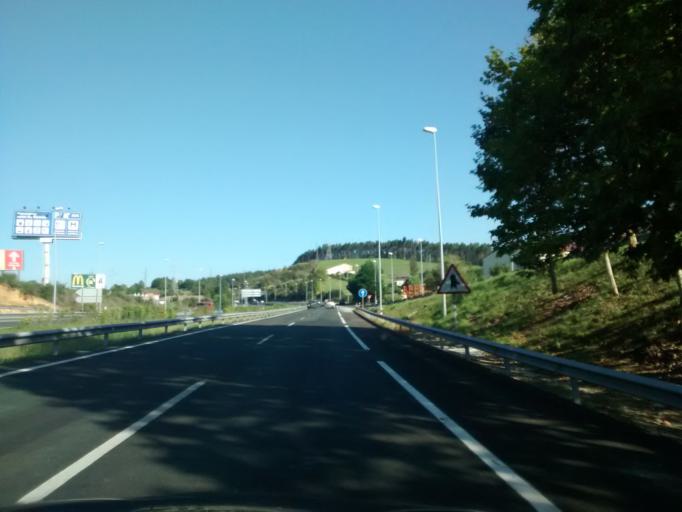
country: ES
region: Cantabria
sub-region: Provincia de Cantabria
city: Reocin
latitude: 43.3545
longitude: -4.0930
